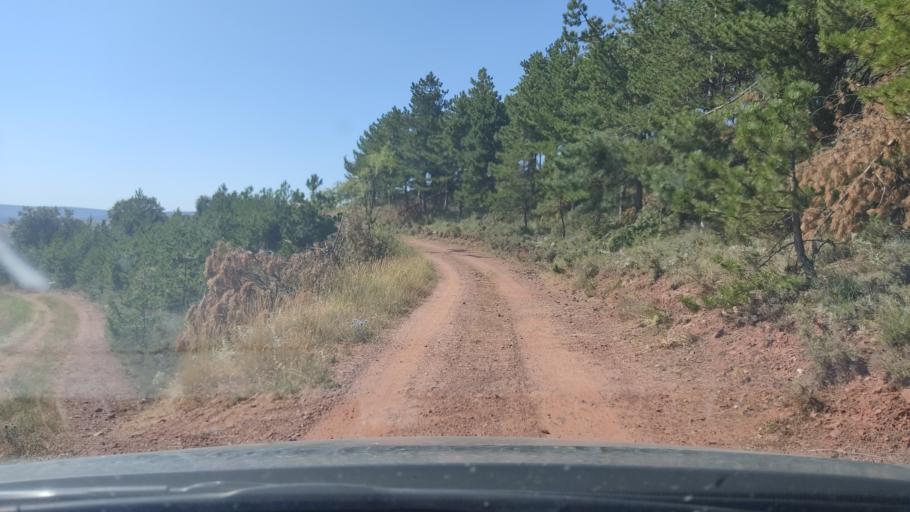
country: ES
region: Aragon
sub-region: Provincia de Teruel
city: Monforte de Moyuela
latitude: 41.0427
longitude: -1.0354
